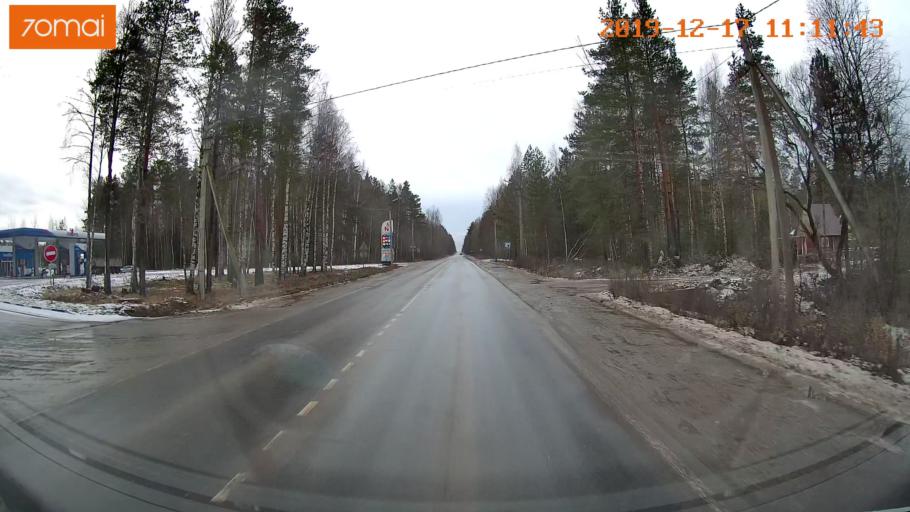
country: RU
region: Vladimir
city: Gus'-Khrustal'nyy
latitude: 55.5844
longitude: 40.6351
